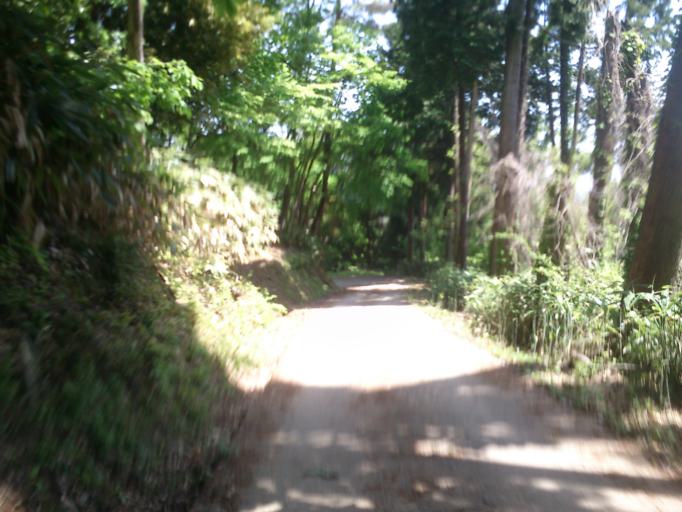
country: JP
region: Kyoto
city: Miyazu
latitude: 35.6089
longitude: 135.1961
